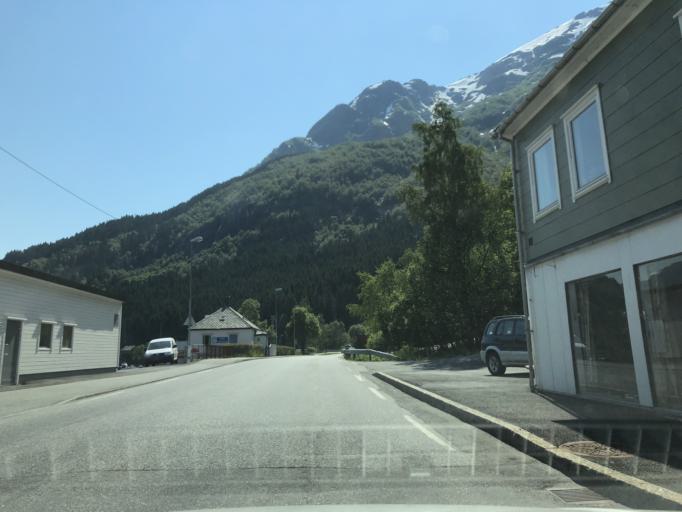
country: NO
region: Hordaland
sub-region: Odda
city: Odda
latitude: 60.0815
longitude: 6.5307
